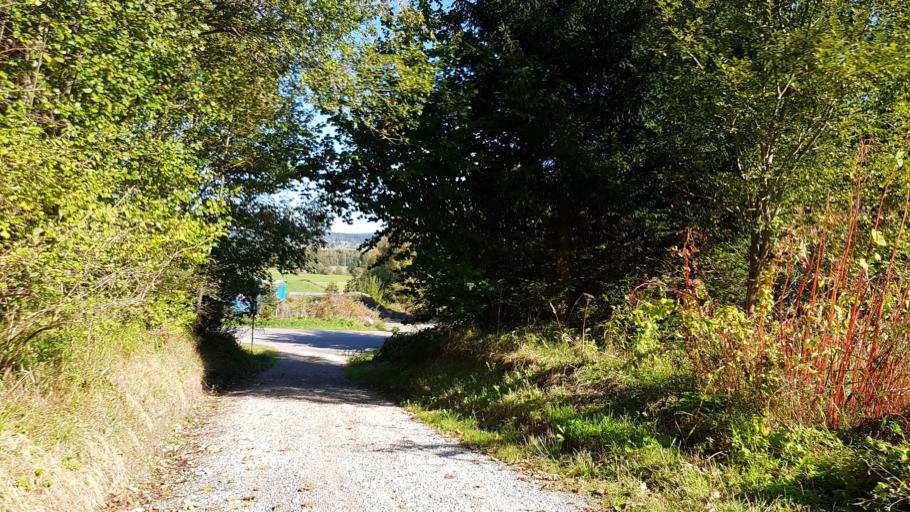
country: DE
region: Bavaria
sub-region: Swabia
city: Fuessen
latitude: 47.5794
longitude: 10.6898
